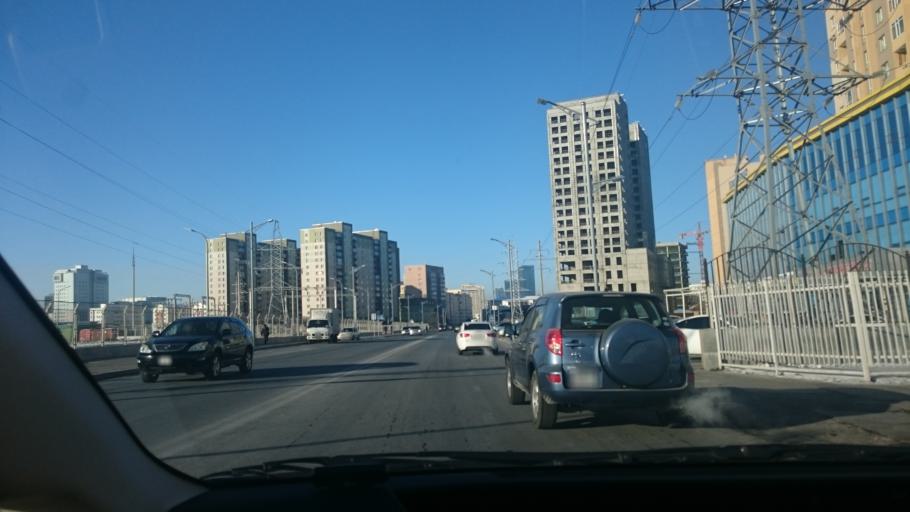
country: MN
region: Ulaanbaatar
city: Ulaanbaatar
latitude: 47.9005
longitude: 106.9303
